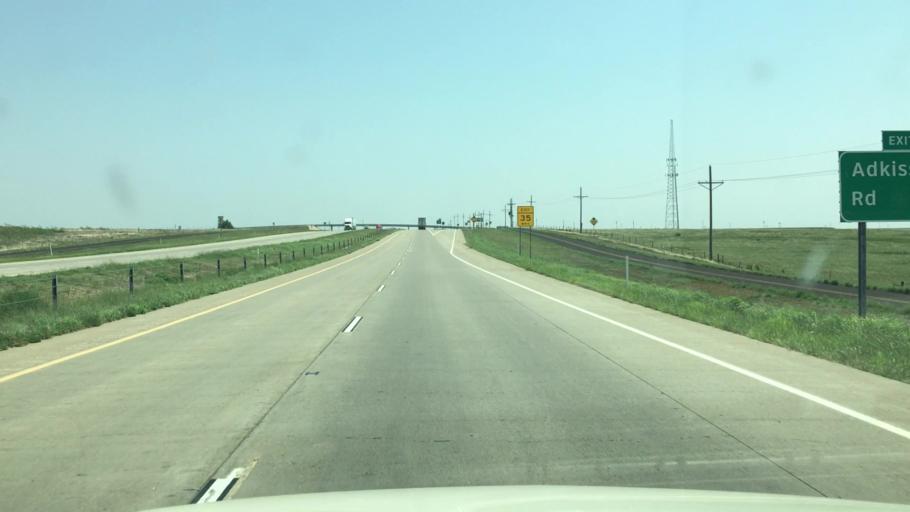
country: US
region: Texas
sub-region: Potter County
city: Bushland
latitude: 35.1980
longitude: -102.1235
